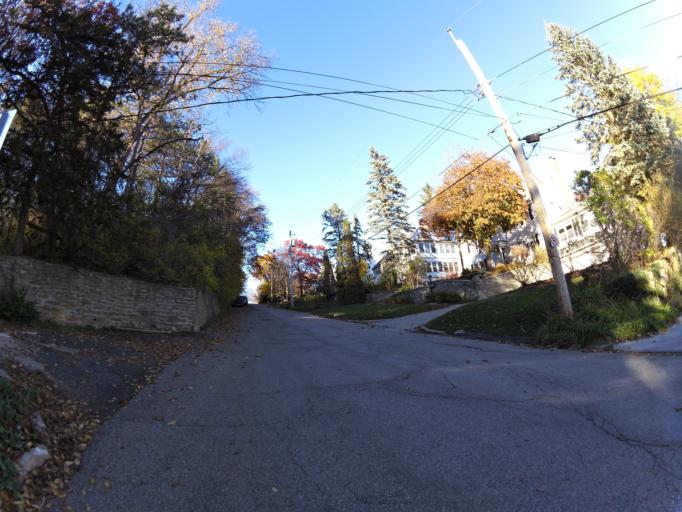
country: US
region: Minnesota
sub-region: Olmsted County
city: Rochester
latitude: 44.0126
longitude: -92.4762
